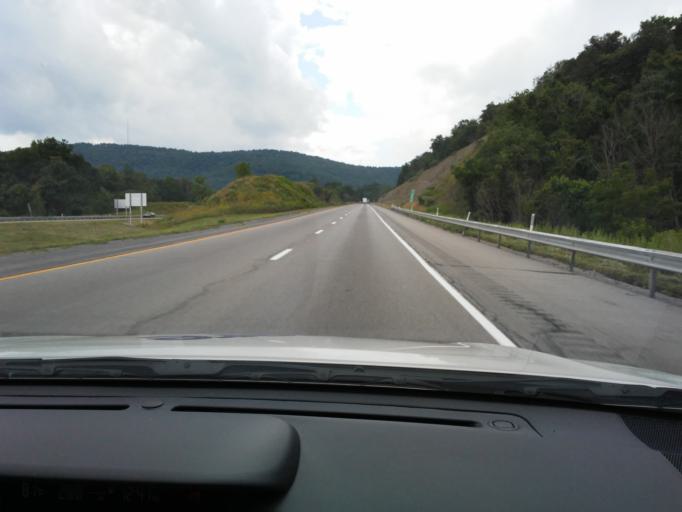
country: US
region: Pennsylvania
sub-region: Centre County
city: Milesburg
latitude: 40.9941
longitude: -77.8431
